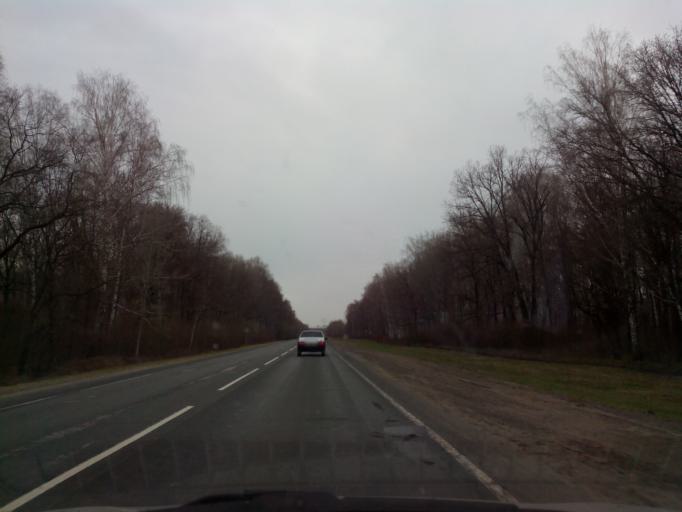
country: RU
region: Tambov
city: Michurinsk
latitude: 53.0726
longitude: 40.4275
